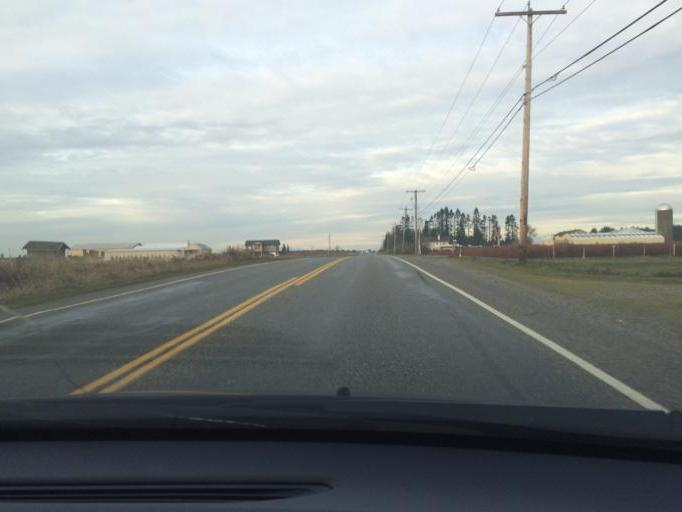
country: US
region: Washington
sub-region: Whatcom County
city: Ferndale
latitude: 48.9273
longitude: -122.5745
